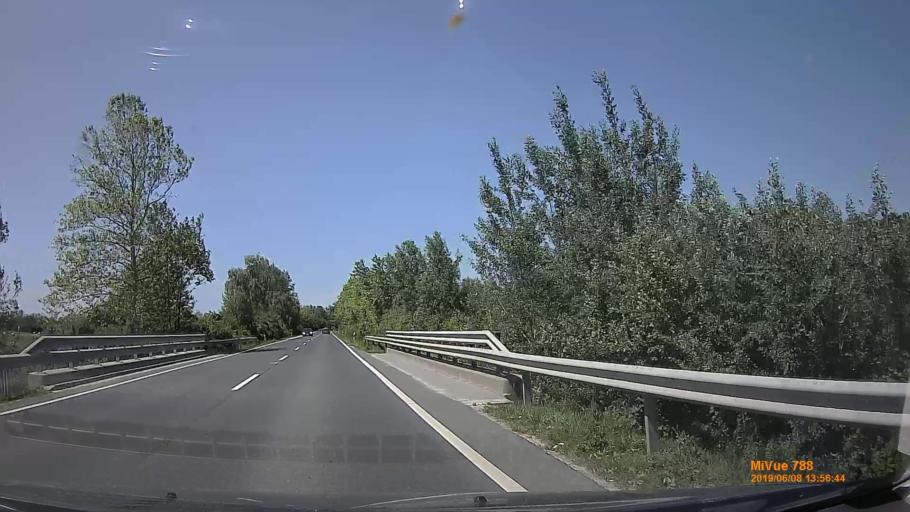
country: HU
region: Vas
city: Sarvar
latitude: 47.3650
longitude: 16.8923
